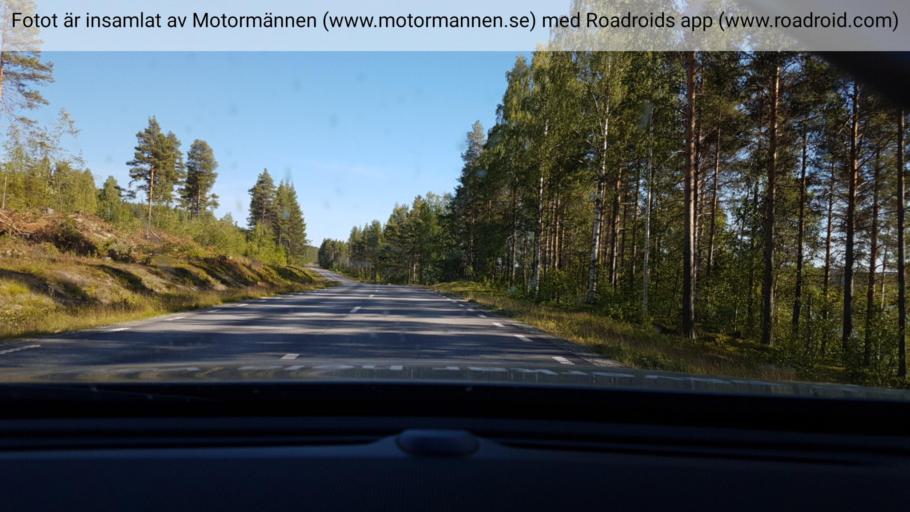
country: SE
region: Vaesterbotten
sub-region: Lycksele Kommun
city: Lycksele
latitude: 64.5503
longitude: 18.7365
